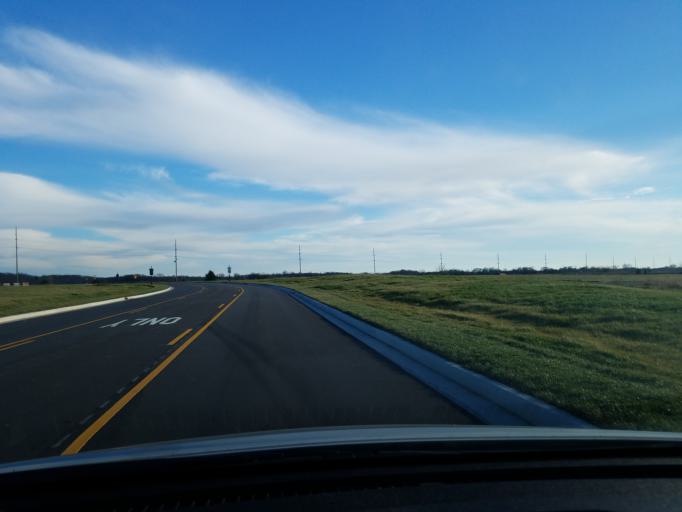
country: US
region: Kentucky
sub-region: Jefferson County
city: Prospect
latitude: 38.3865
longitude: -85.6660
